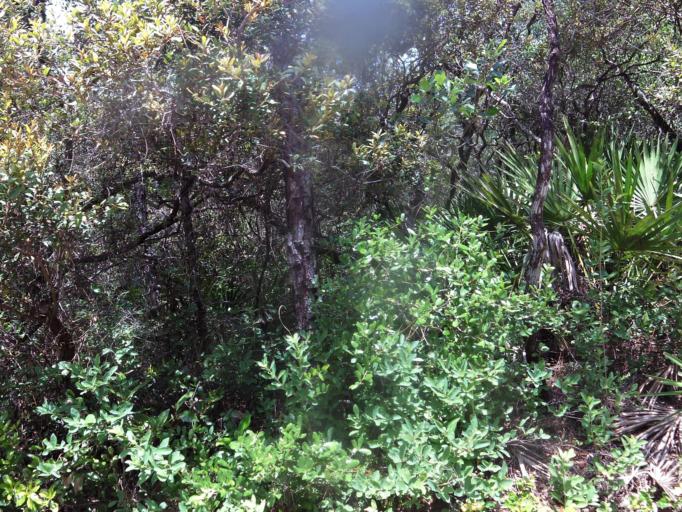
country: US
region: Florida
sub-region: Nassau County
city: Fernandina Beach
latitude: 30.4972
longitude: -81.4921
